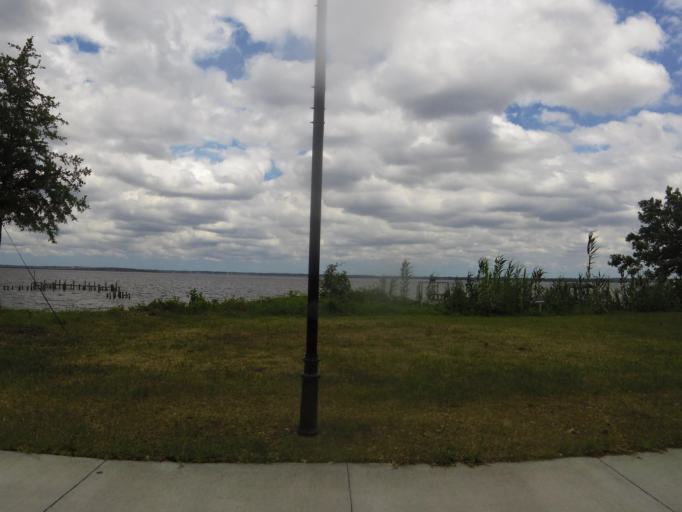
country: US
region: Florida
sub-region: Clay County
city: Orange Park
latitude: 30.1807
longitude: -81.6983
